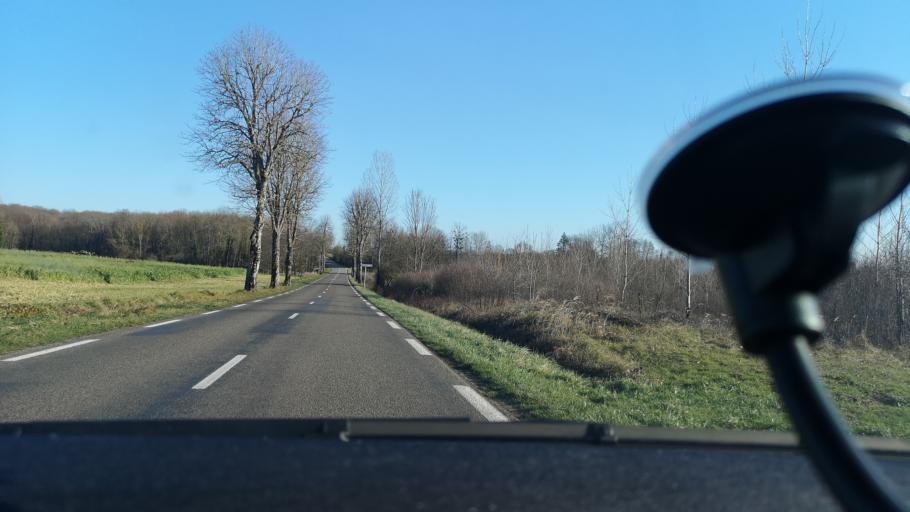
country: FR
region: Franche-Comte
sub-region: Departement du Jura
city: Bletterans
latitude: 46.7442
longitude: 5.4169
